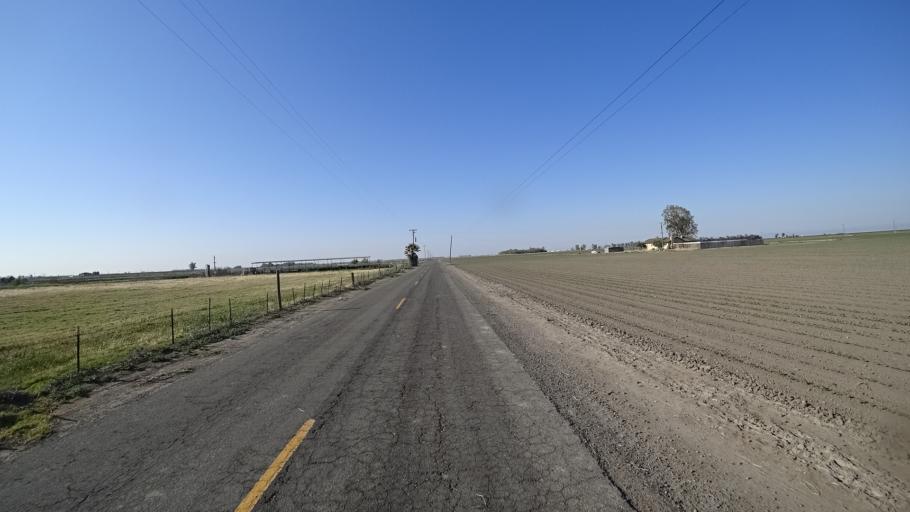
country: US
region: California
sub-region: Fresno County
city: Riverdale
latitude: 36.3888
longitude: -119.9277
